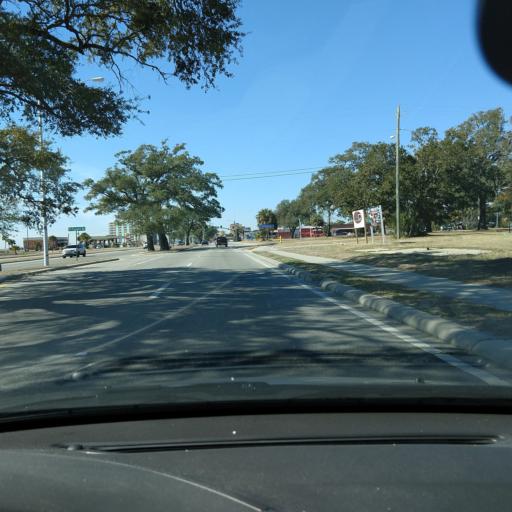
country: US
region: Mississippi
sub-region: Harrison County
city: Biloxi
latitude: 30.3938
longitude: -88.9449
